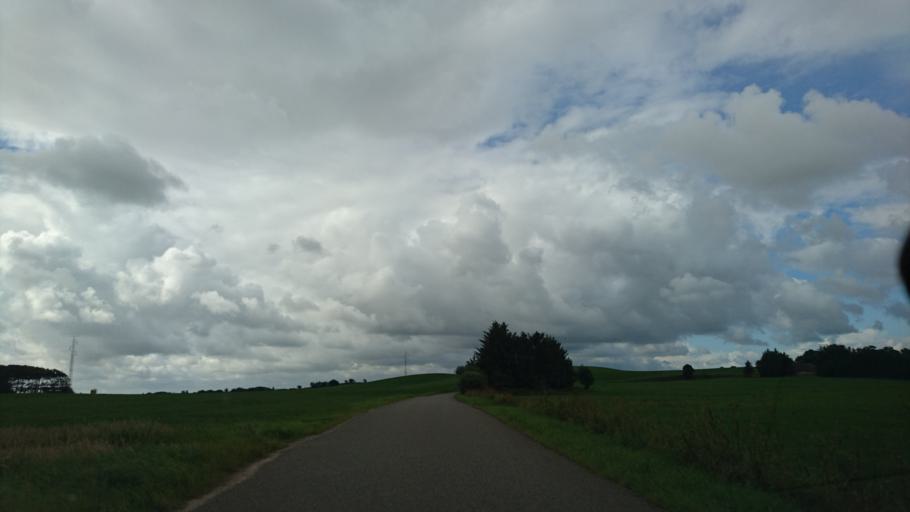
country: DK
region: North Denmark
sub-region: Hjorring Kommune
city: Tars
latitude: 57.3709
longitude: 10.2105
